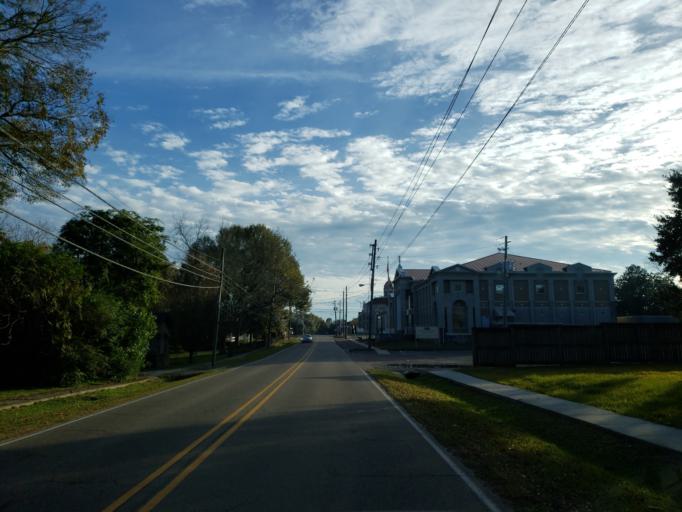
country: US
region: Mississippi
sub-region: Lamar County
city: Purvis
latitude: 31.1464
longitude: -89.4120
